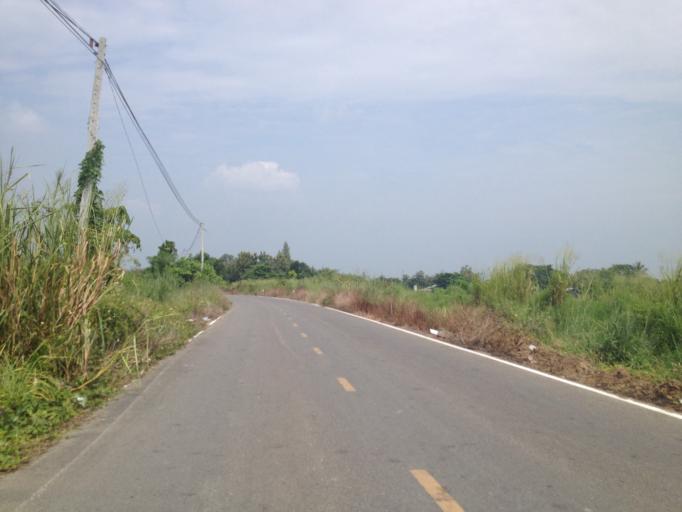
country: TH
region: Chiang Mai
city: San Pa Tong
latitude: 18.6526
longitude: 98.8701
